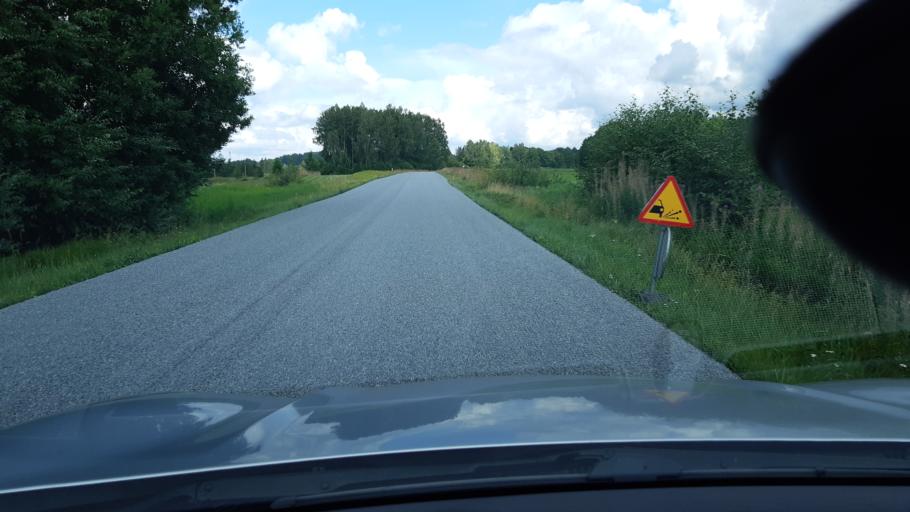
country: EE
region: Raplamaa
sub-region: Kehtna vald
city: Kehtna
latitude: 58.8996
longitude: 25.0278
